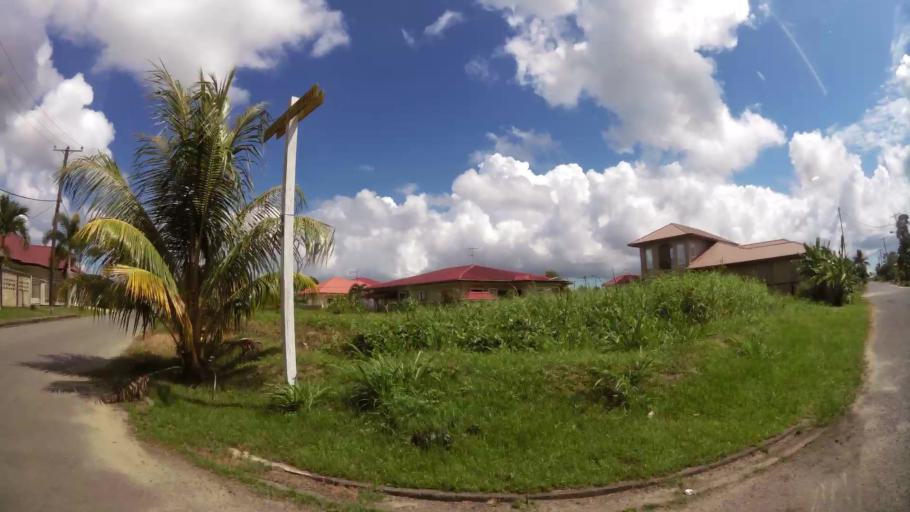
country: SR
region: Paramaribo
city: Paramaribo
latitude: 5.8624
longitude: -55.1336
